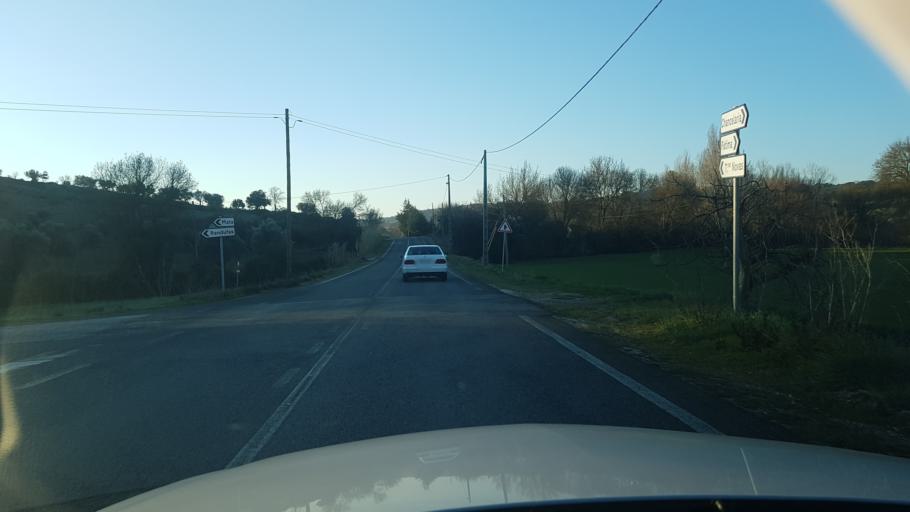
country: PT
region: Santarem
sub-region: Torres Novas
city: Torres Novas
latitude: 39.5277
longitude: -8.5508
